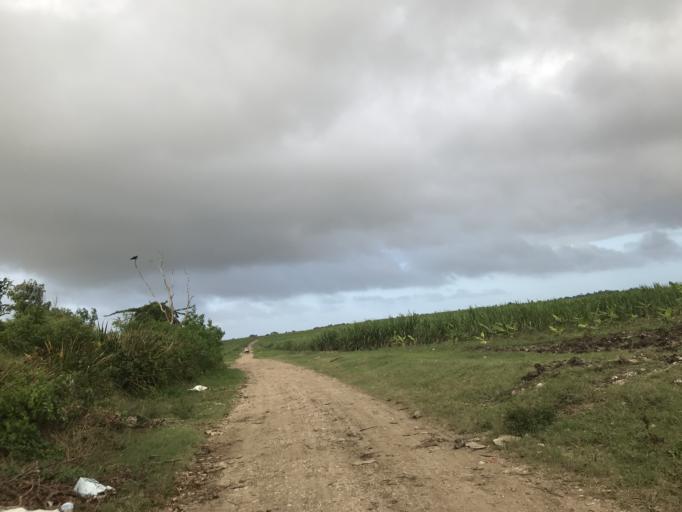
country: CU
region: Villa Clara
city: Camajuani
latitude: 22.4718
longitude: -79.7192
